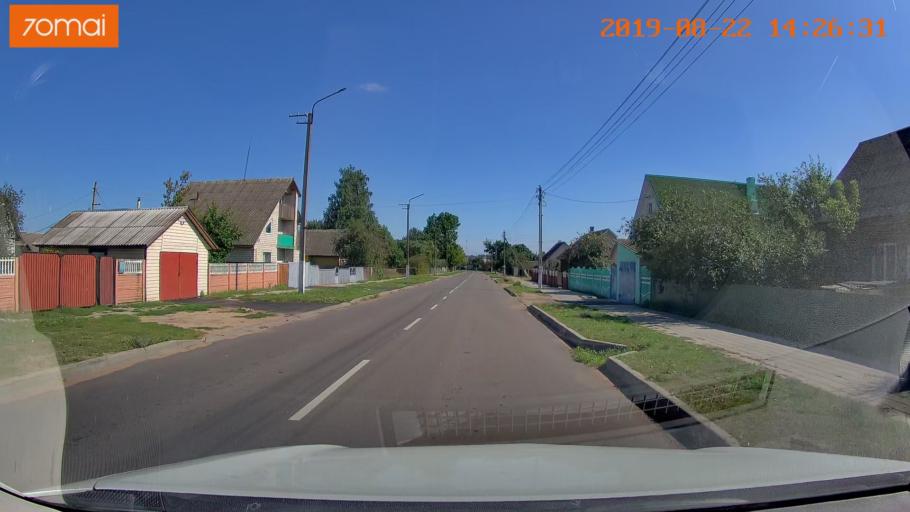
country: BY
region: Mogilev
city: Asipovichy
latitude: 53.2990
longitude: 28.6162
